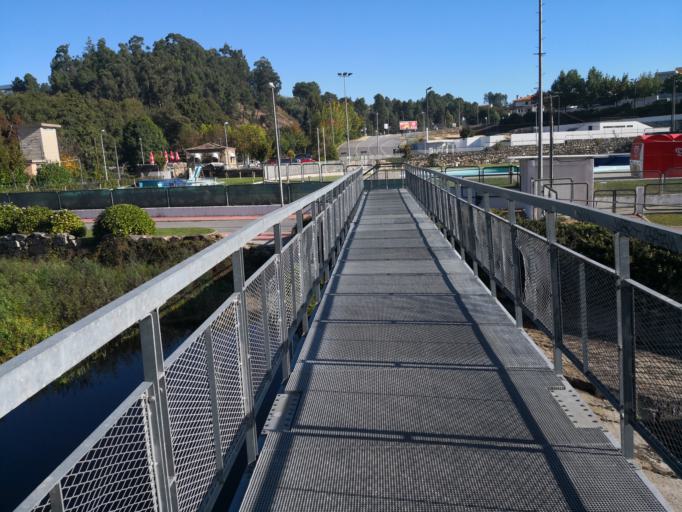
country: PT
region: Vila Real
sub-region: Vila Real
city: Vila Real
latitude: 41.3041
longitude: -7.7358
